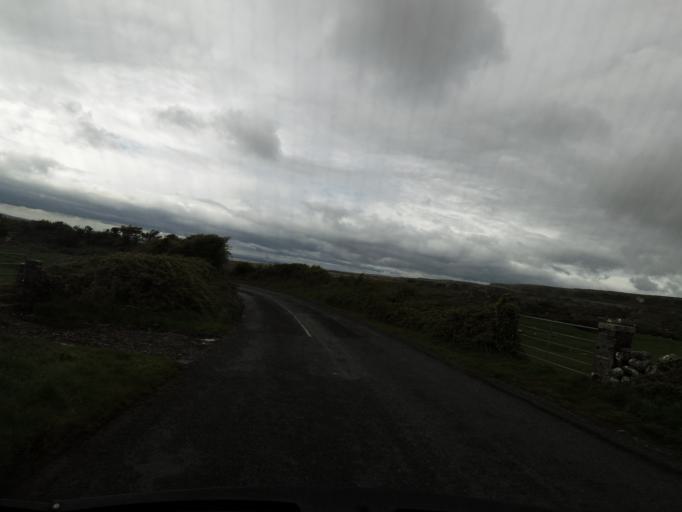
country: IE
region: Connaught
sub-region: County Galway
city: Bearna
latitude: 53.0520
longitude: -9.3414
